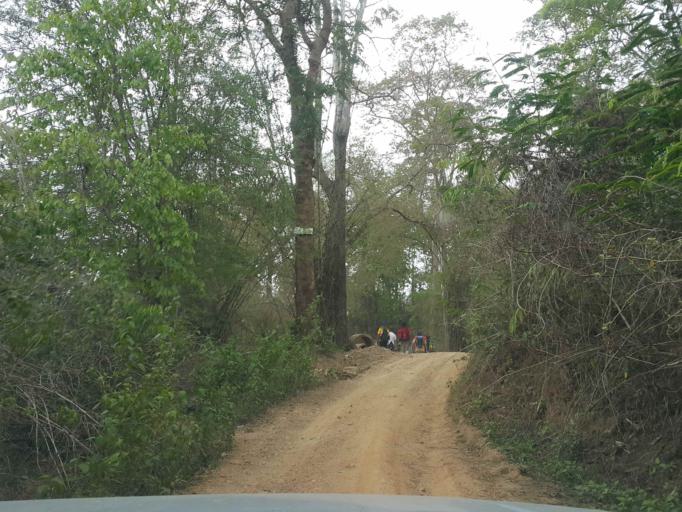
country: TH
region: Chiang Mai
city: Wiang Haeng
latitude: 19.3665
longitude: 98.7179
